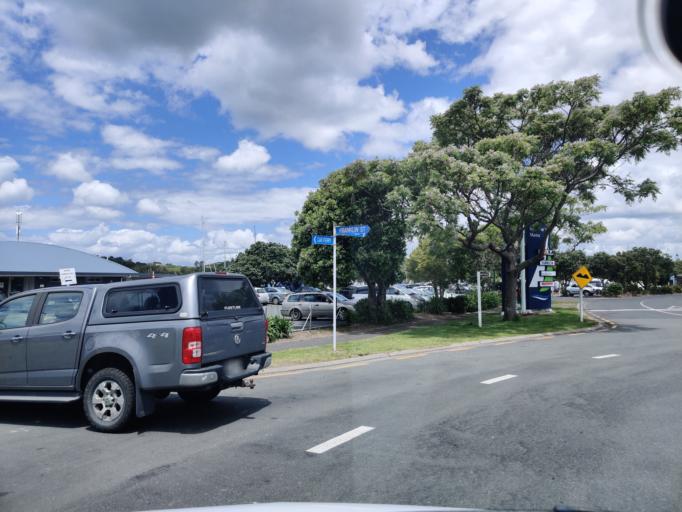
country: NZ
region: Northland
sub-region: Far North District
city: Paihia
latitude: -35.3127
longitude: 174.1213
